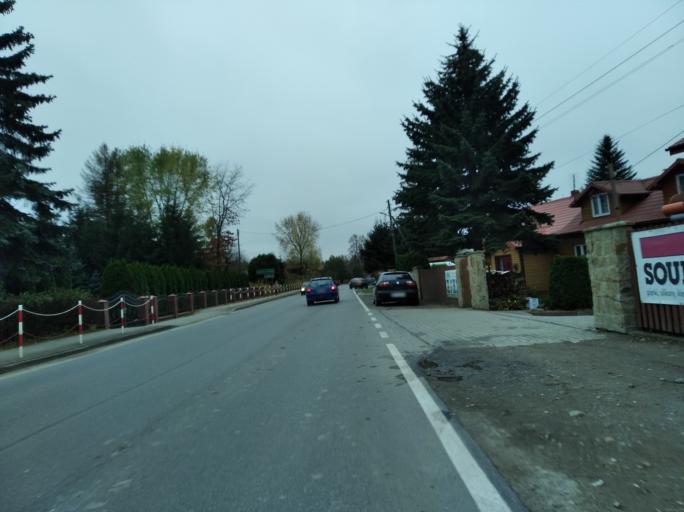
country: PL
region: Subcarpathian Voivodeship
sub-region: Powiat krosnienski
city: Chorkowka
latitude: 49.6704
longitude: 21.6936
